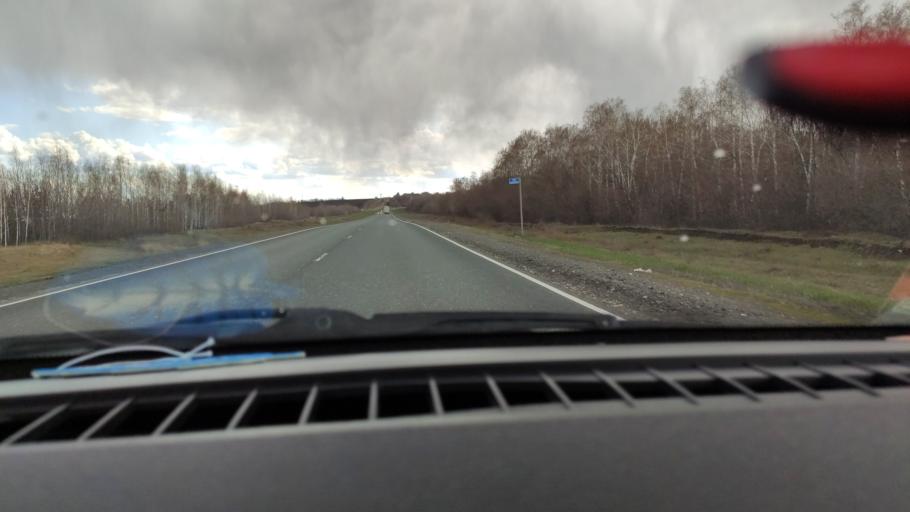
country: RU
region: Saratov
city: Balakovo
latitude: 52.1387
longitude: 47.7987
